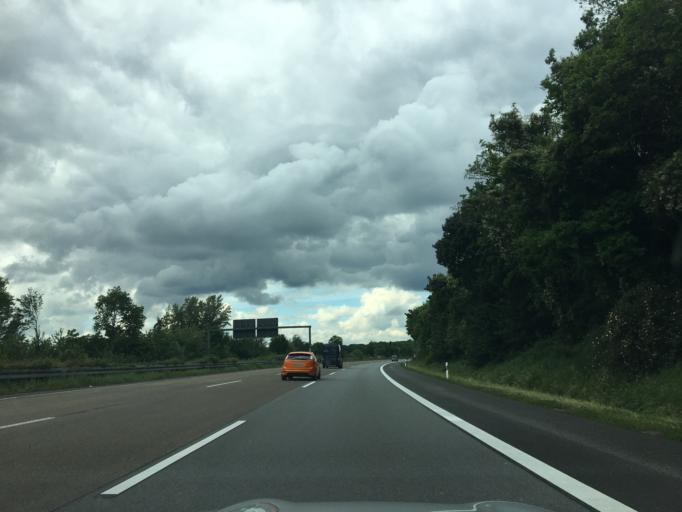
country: DE
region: Hesse
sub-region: Regierungsbezirk Darmstadt
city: Maintal
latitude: 50.1425
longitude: 8.7936
